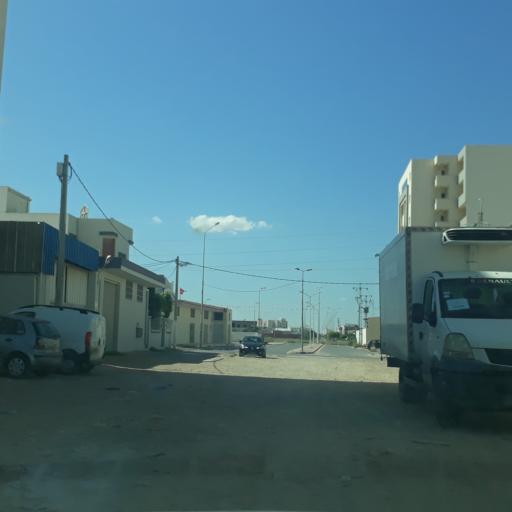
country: TN
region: Safaqis
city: Al Qarmadah
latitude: 34.8334
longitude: 10.7631
